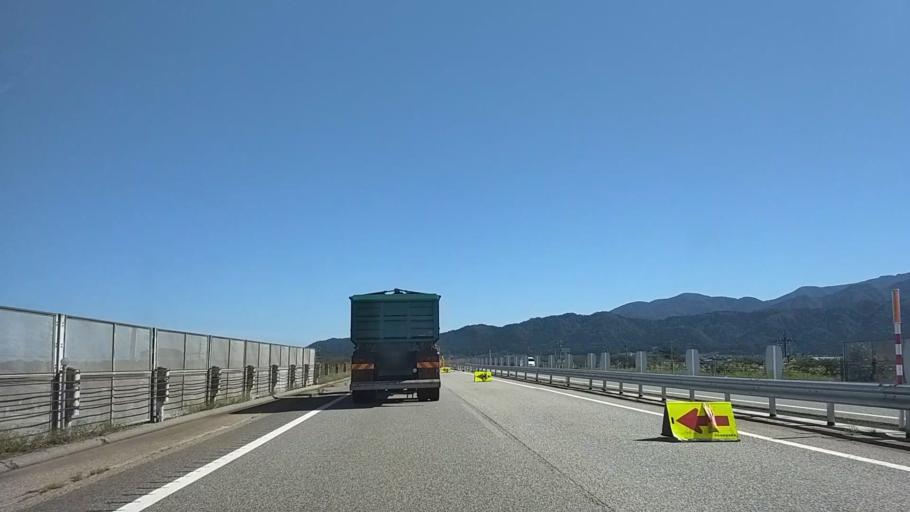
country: JP
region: Toyama
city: Nyuzen
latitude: 36.9324
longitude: 137.5356
